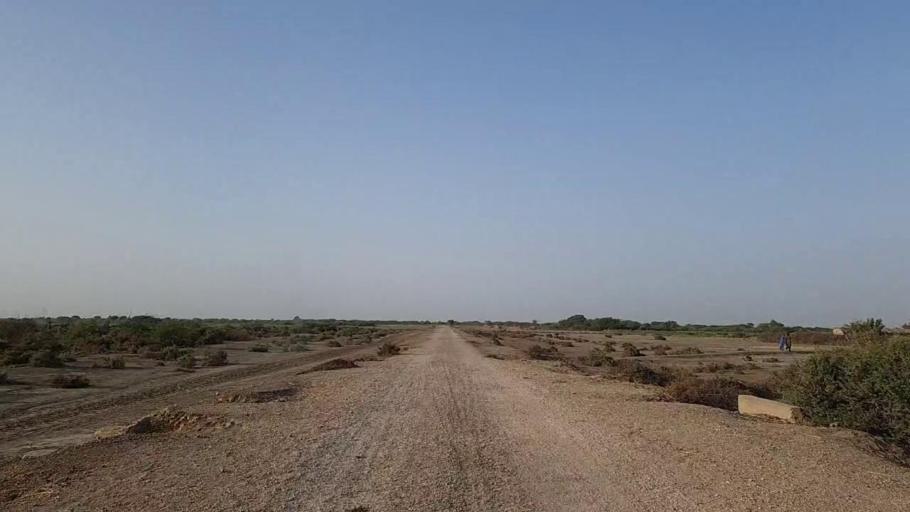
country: PK
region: Sindh
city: Jati
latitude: 24.3760
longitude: 68.1478
